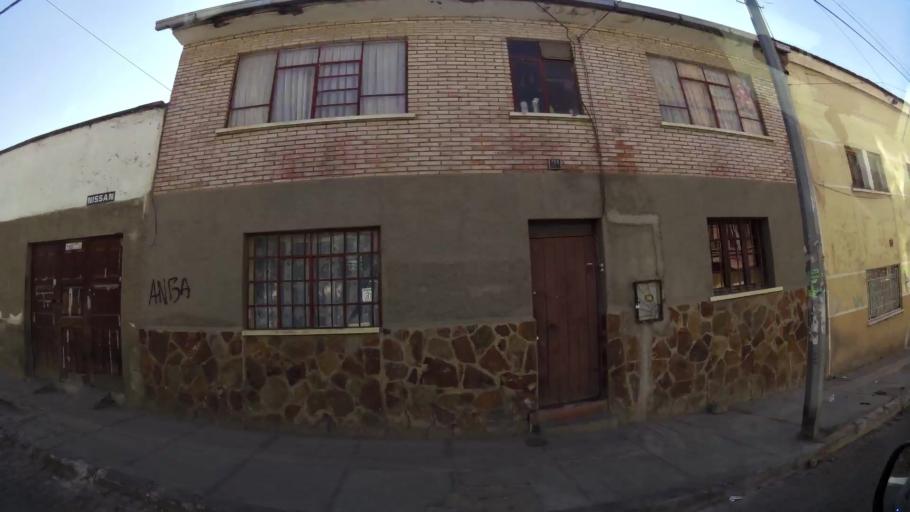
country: BO
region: La Paz
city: La Paz
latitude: -16.5074
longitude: -68.1345
